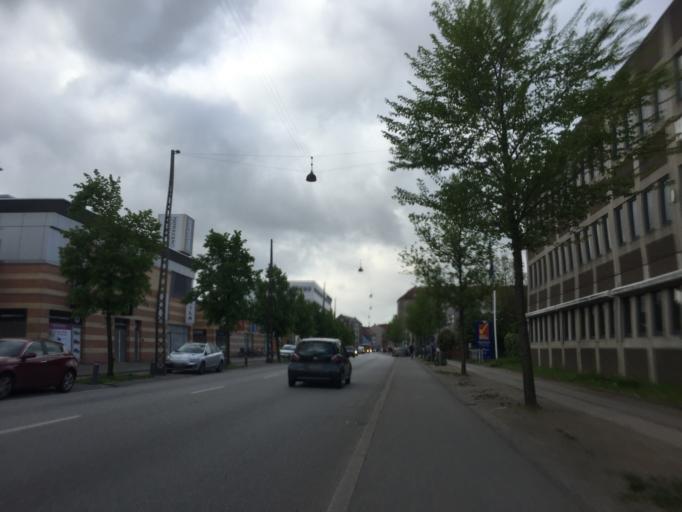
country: DK
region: Capital Region
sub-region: Frederiksberg Kommune
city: Frederiksberg
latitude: 55.7037
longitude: 12.5378
